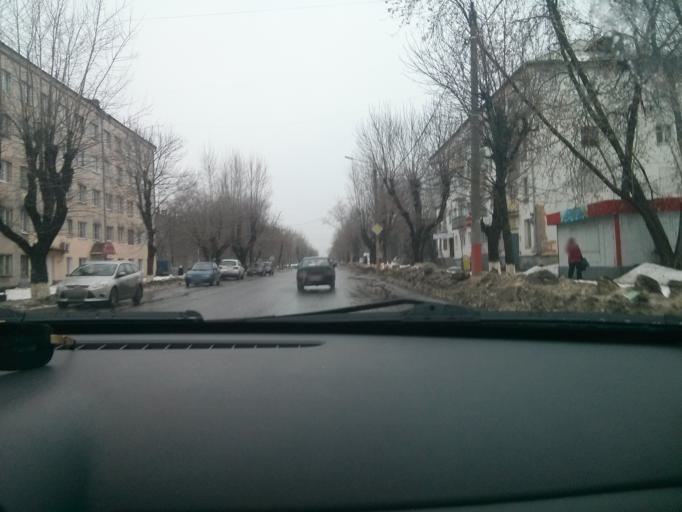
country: RU
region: Vladimir
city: Murom
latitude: 55.5662
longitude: 42.0571
